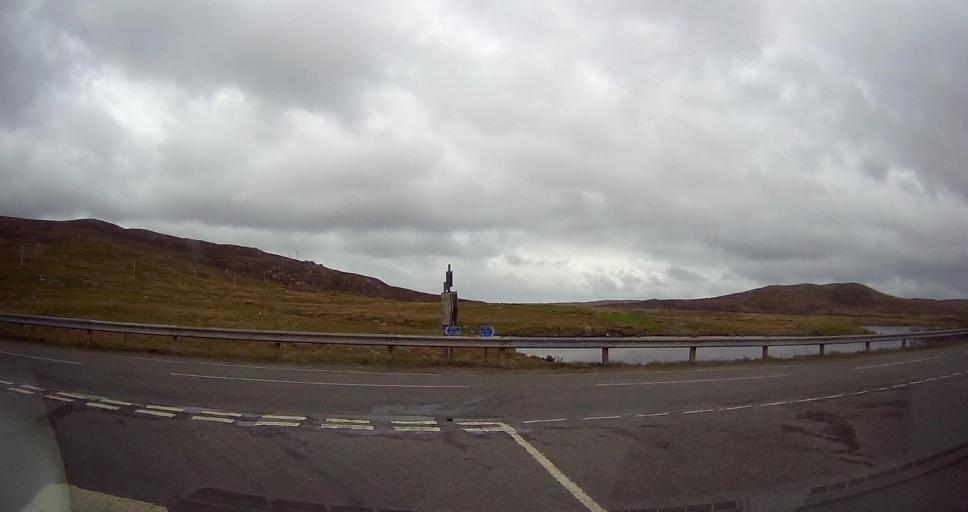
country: GB
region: Scotland
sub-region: Shetland Islands
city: Lerwick
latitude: 60.3491
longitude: -1.2543
